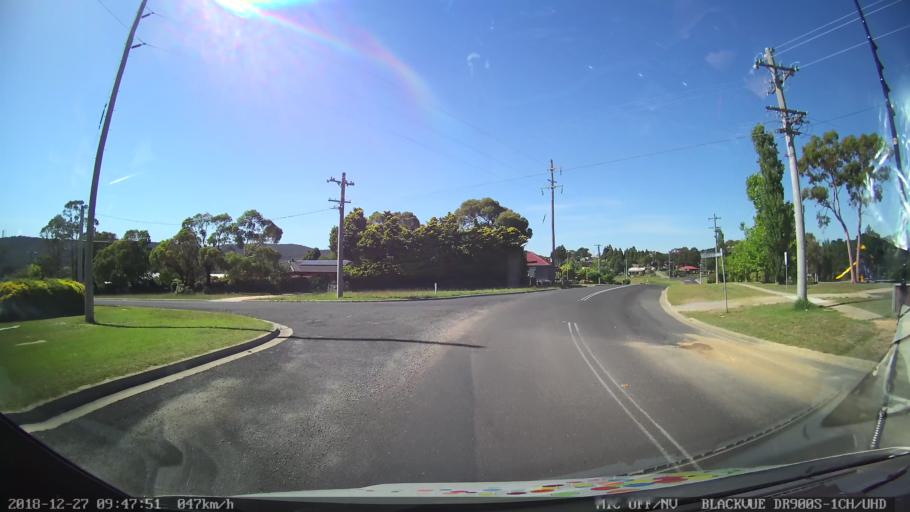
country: AU
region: New South Wales
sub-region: Lithgow
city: Portland
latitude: -33.3498
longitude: 149.9896
